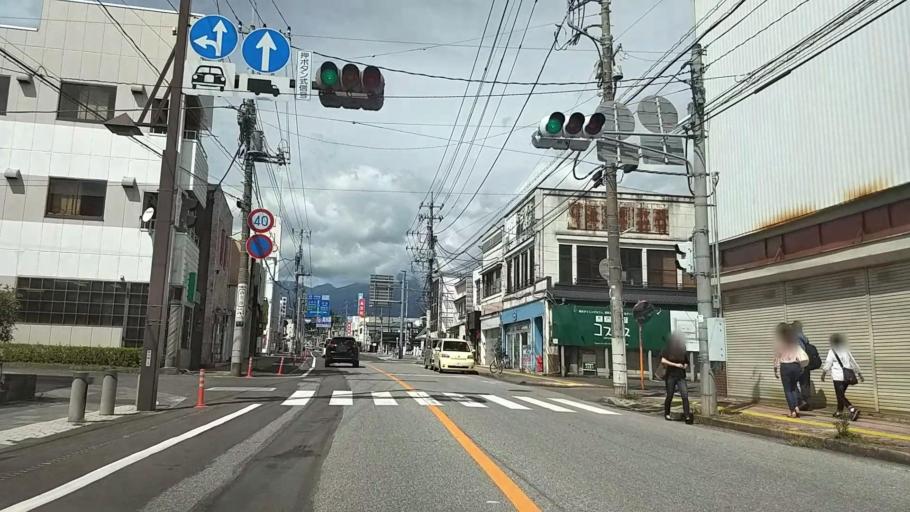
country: JP
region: Tochigi
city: Imaichi
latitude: 36.7237
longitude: 139.6888
